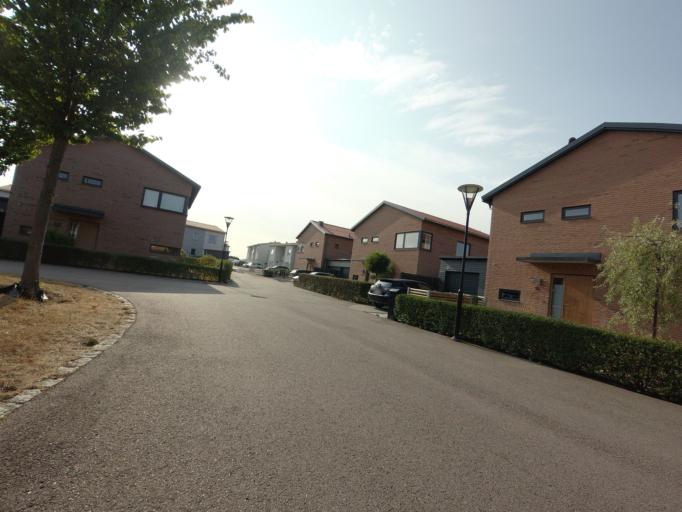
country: SE
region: Skane
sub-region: Hoganas Kommun
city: Hoganas
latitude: 56.1531
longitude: 12.5826
